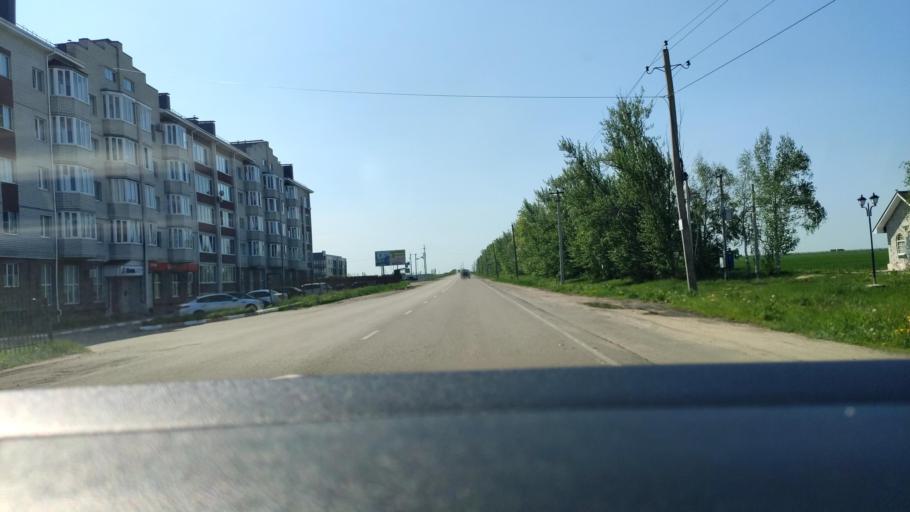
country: RU
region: Voronezj
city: Novaya Usman'
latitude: 51.6023
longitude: 39.3734
